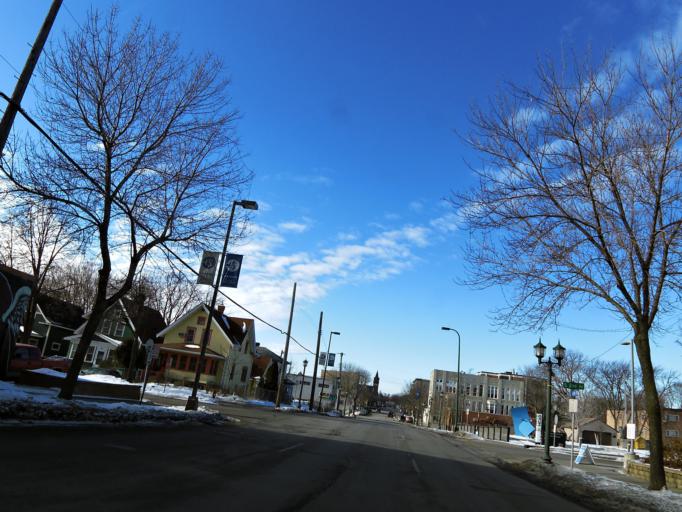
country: US
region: Minnesota
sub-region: Hennepin County
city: Minneapolis
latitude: 44.9556
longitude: -93.2735
